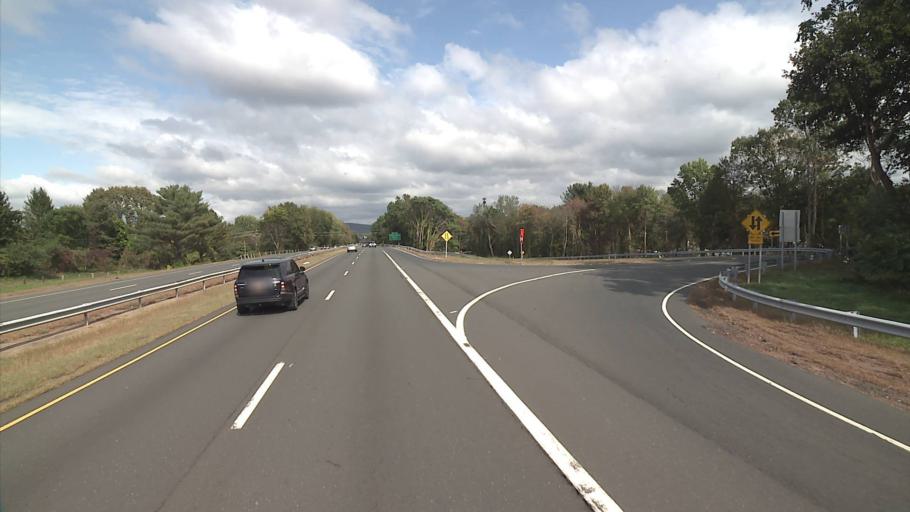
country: US
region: Connecticut
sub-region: New Haven County
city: Meriden
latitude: 41.5110
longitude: -72.7832
